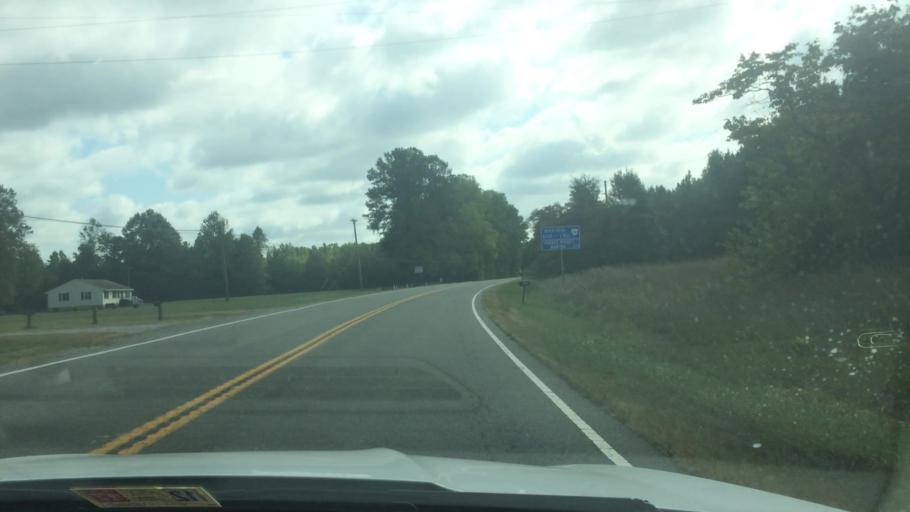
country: US
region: Virginia
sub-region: Lancaster County
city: Lancaster
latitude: 37.8380
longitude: -76.5774
